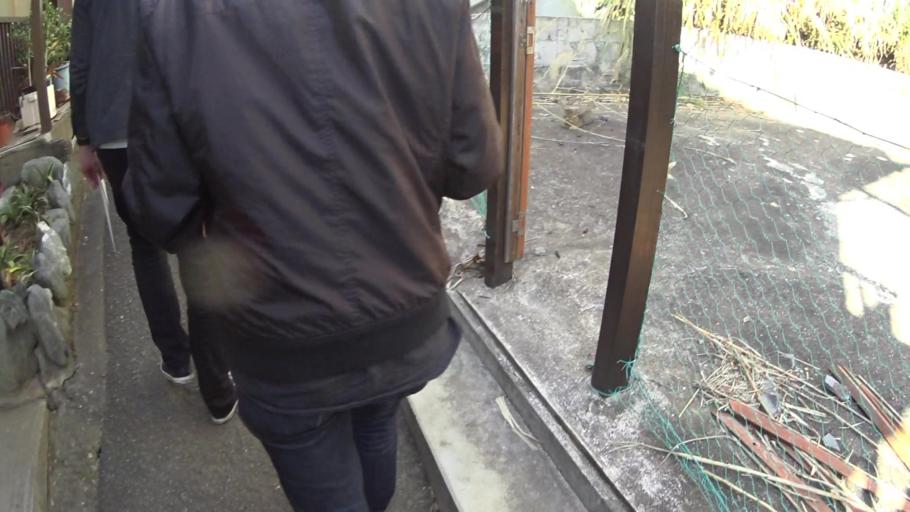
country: JP
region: Wakayama
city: Minato
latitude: 34.1887
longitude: 135.1431
